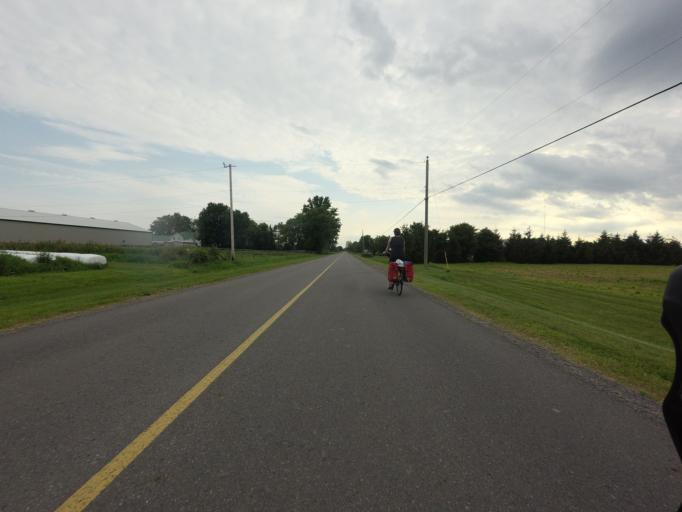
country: CA
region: Ontario
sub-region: Lanark County
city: Smiths Falls
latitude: 45.0027
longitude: -75.7508
